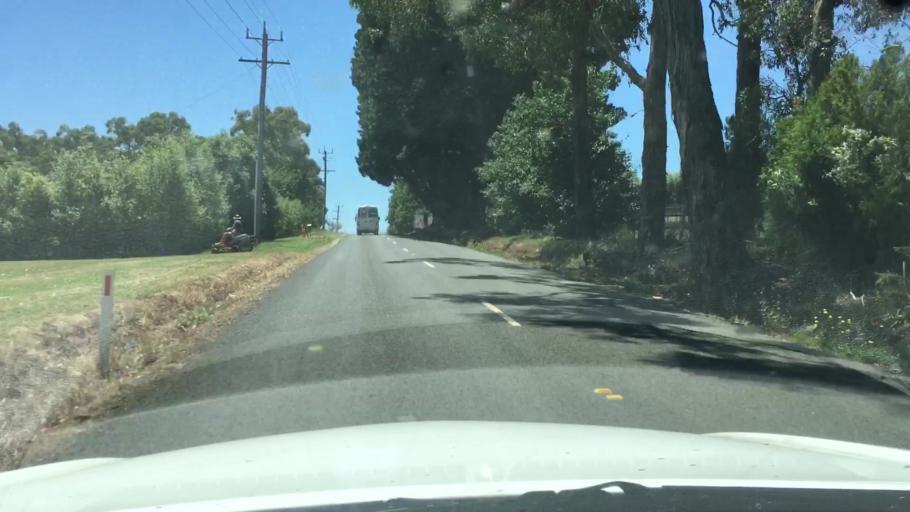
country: AU
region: Victoria
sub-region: Yarra Ranges
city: Mount Evelyn
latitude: -37.7988
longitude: 145.4496
